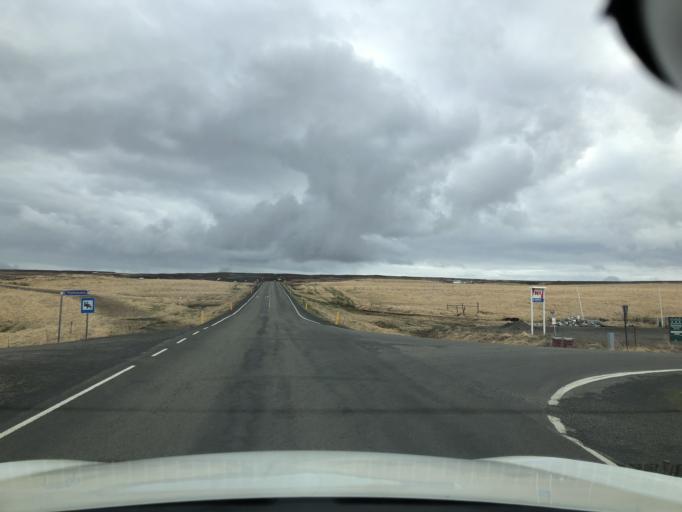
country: IS
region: Northeast
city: Laugar
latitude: 65.6866
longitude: -17.5395
